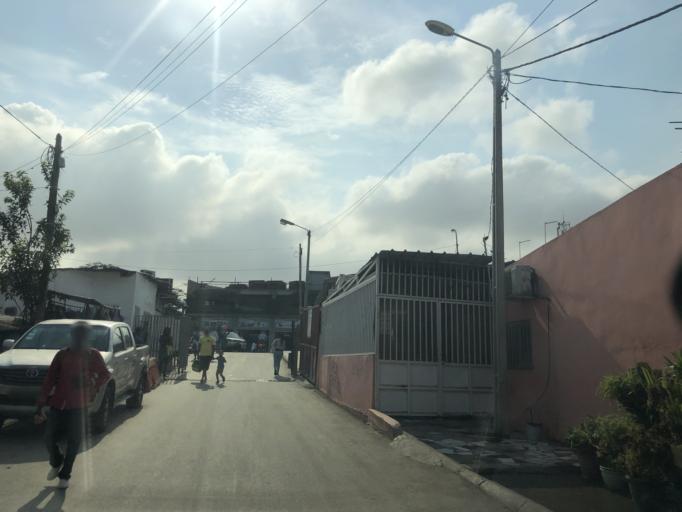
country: AO
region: Luanda
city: Luanda
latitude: -8.8291
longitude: 13.2255
